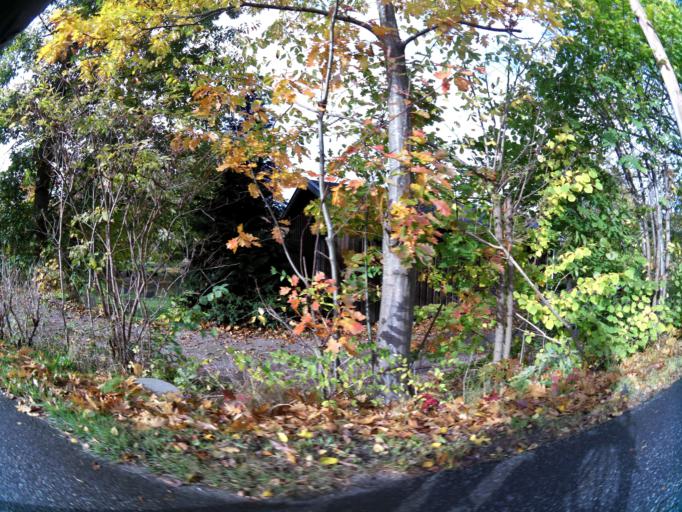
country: NO
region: Ostfold
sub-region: Fredrikstad
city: Fredrikstad
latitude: 59.2266
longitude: 10.9582
